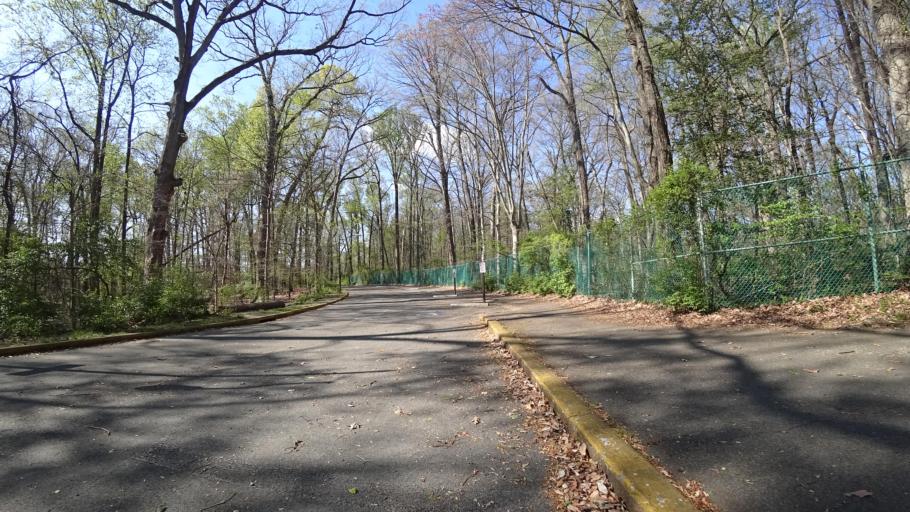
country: US
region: Maryland
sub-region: Montgomery County
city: Chevy Chase
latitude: 38.9509
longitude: -77.0403
